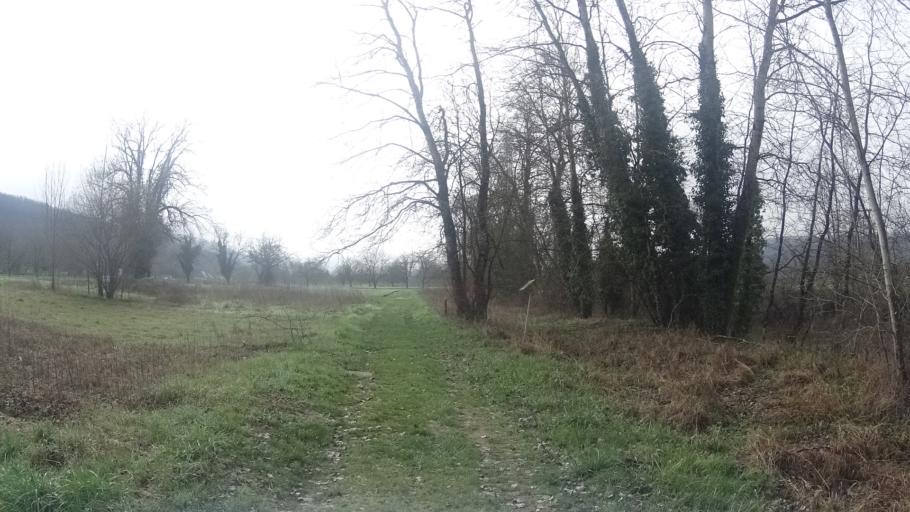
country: FR
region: Aquitaine
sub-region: Departement de la Dordogne
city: Montignac
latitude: 45.1096
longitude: 1.2227
